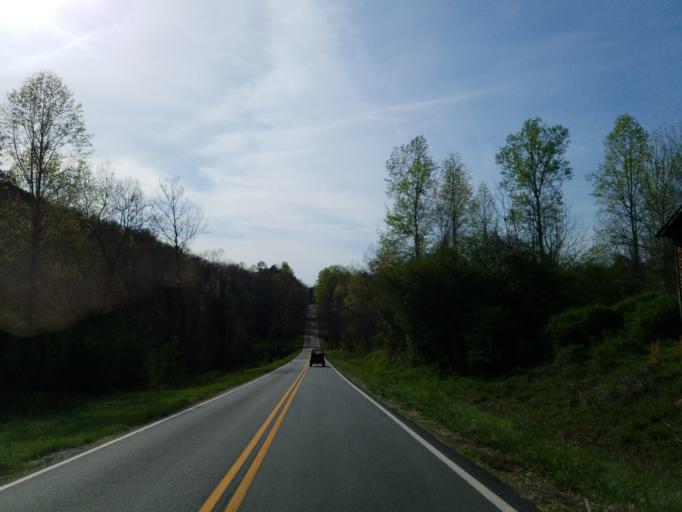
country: US
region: Georgia
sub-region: Lumpkin County
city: Dahlonega
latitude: 34.4746
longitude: -84.0240
